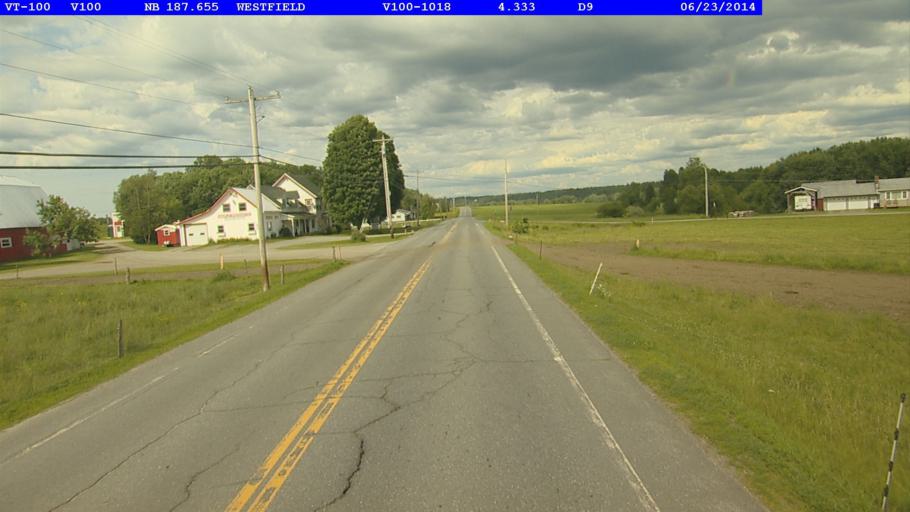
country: US
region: Vermont
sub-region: Orleans County
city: Newport
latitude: 44.8937
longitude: -72.4197
